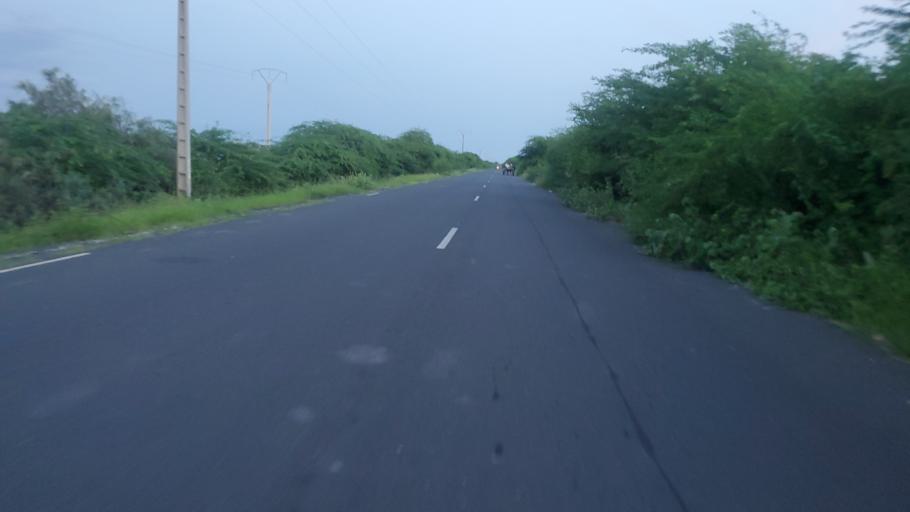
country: SN
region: Saint-Louis
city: Saint-Louis
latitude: 16.0878
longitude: -16.3952
